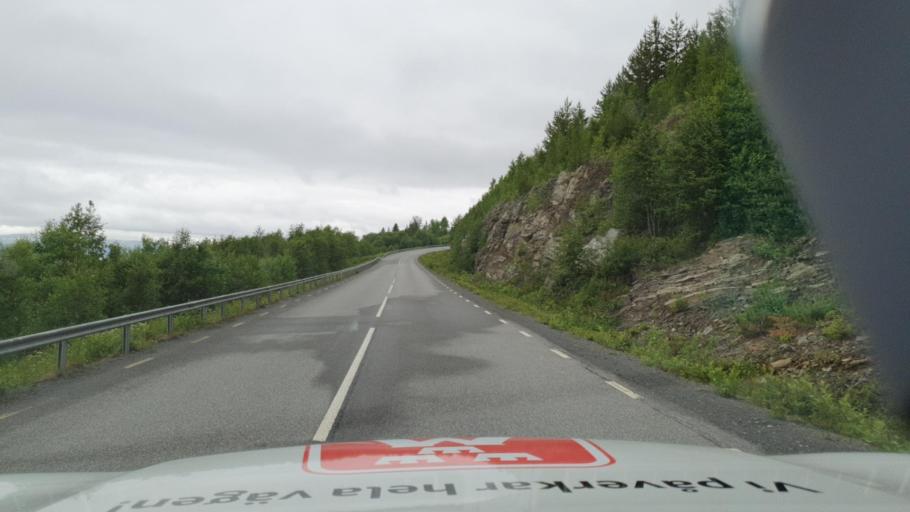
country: SE
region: Jaemtland
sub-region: Are Kommun
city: Are
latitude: 63.6336
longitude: 13.1110
